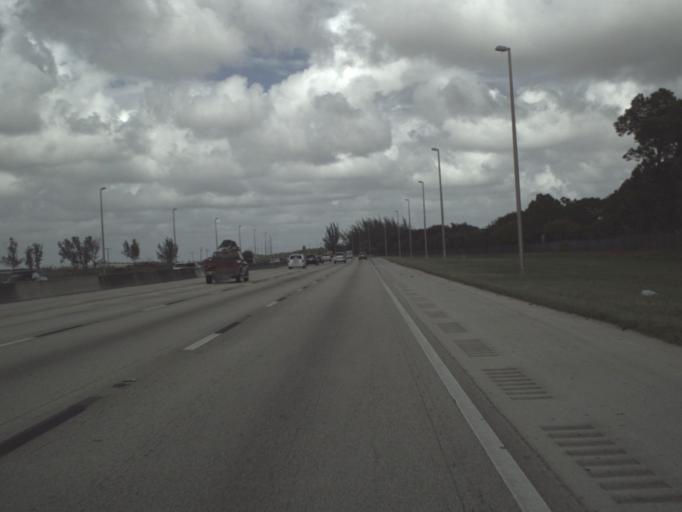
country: US
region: Florida
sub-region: Palm Beach County
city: Villages of Oriole
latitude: 26.4764
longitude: -80.1734
